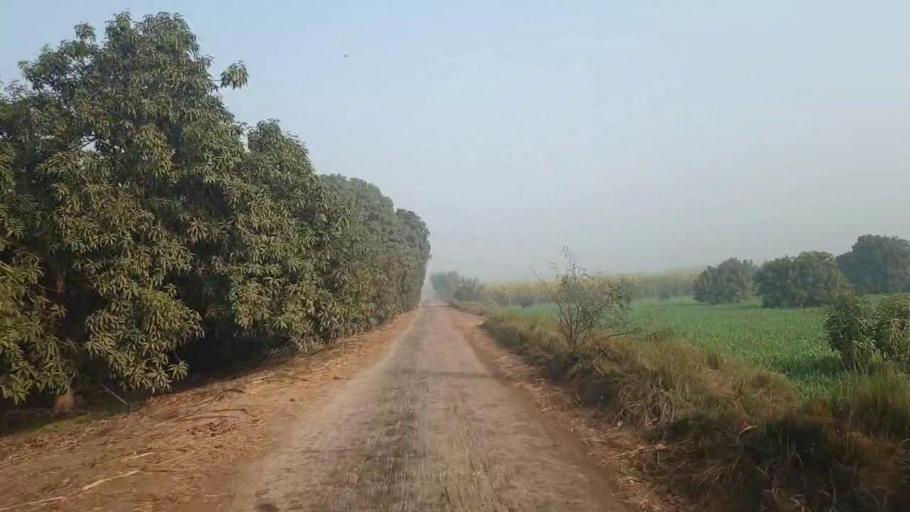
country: PK
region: Sindh
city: Tando Adam
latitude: 25.7961
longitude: 68.6334
